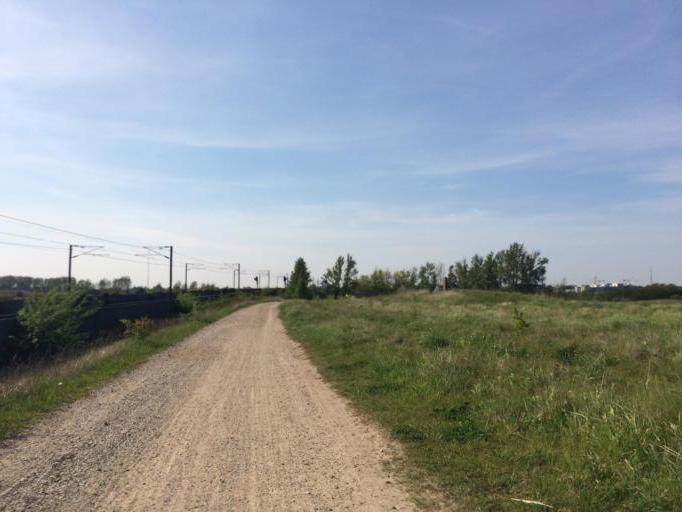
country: DK
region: Capital Region
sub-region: Kobenhavn
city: Copenhagen
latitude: 55.6343
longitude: 12.5572
